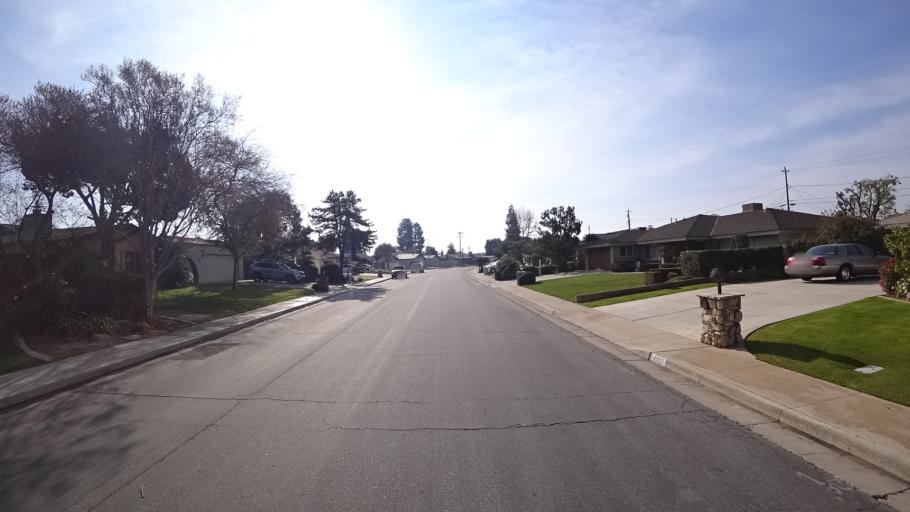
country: US
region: California
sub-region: Kern County
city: Oildale
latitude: 35.4105
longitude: -118.9499
